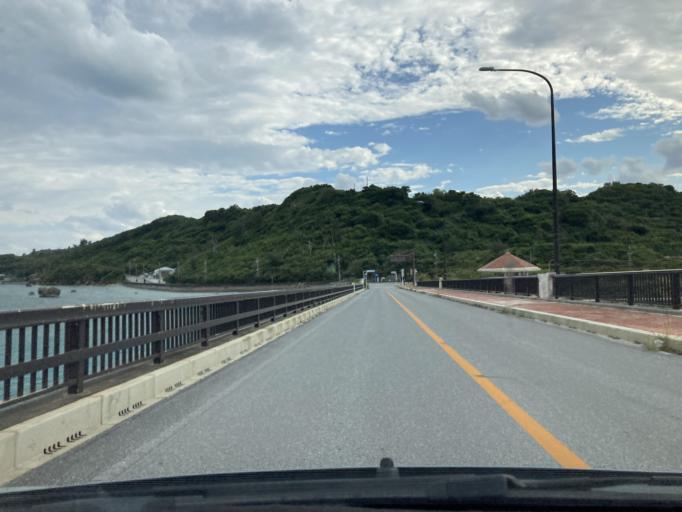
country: JP
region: Okinawa
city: Katsuren-haebaru
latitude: 26.3299
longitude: 127.9568
